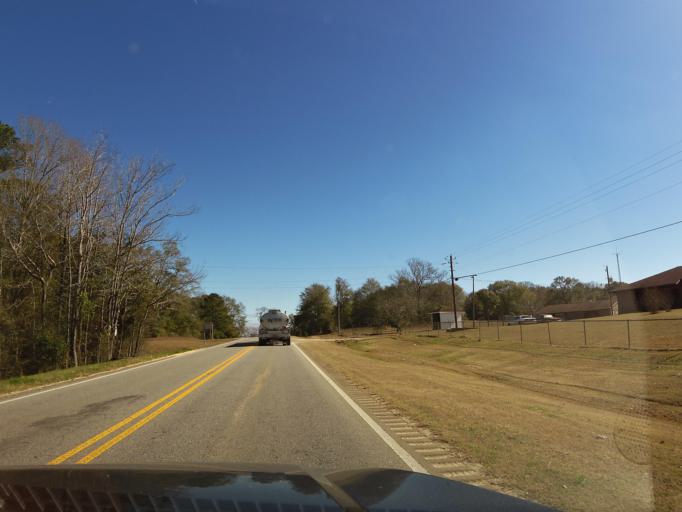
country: US
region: Alabama
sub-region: Bullock County
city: Union Springs
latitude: 32.0800
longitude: -85.5295
